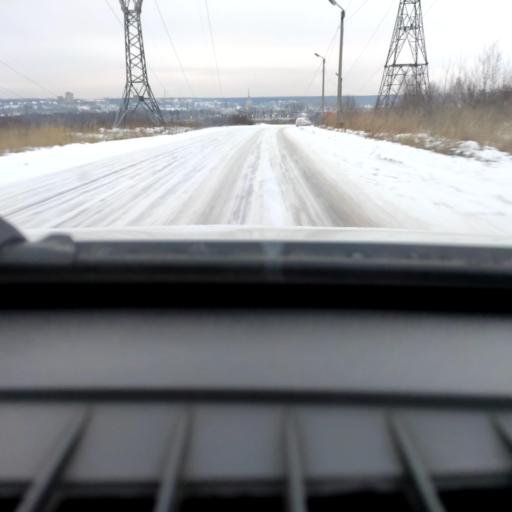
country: RU
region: Perm
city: Perm
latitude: 58.1078
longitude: 56.3666
